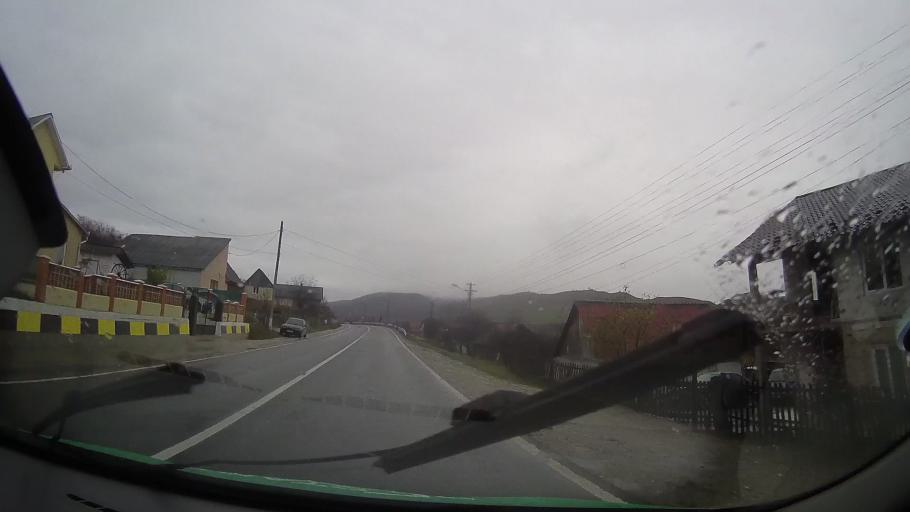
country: RO
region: Bistrita-Nasaud
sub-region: Comuna Galatii Bistritei
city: Galatii Bistritei
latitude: 46.9521
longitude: 24.4489
